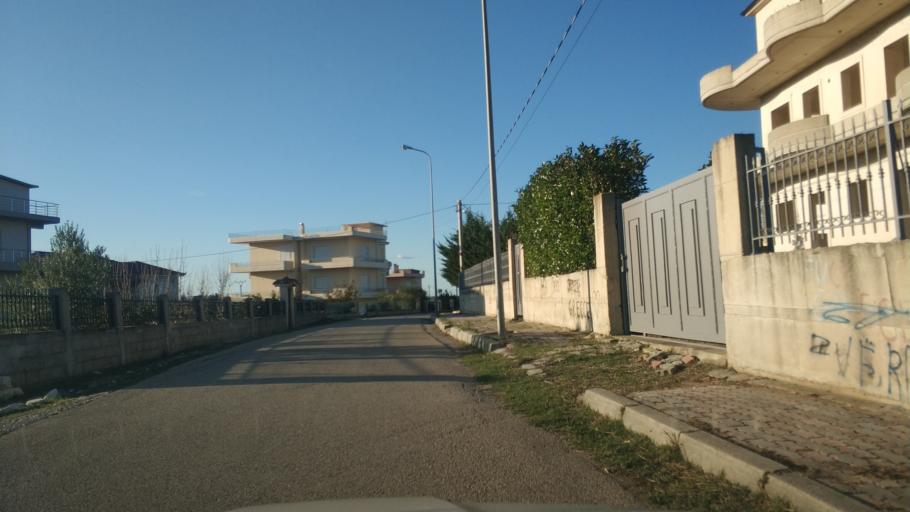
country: AL
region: Vlore
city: Vlore
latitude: 40.5082
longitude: 19.4107
